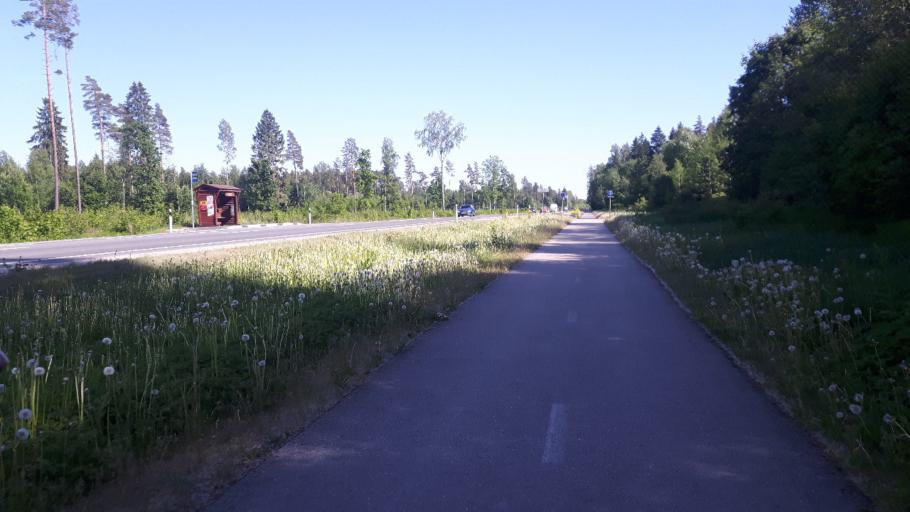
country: EE
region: Raplamaa
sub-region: Kehtna vald
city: Kehtna
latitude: 58.9586
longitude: 24.8649
